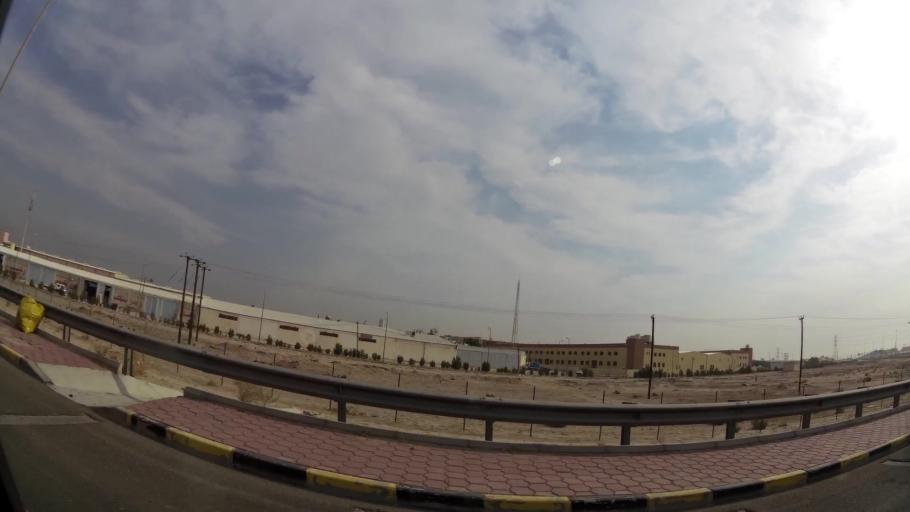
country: KW
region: Muhafazat al Jahra'
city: Al Jahra'
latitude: 29.2968
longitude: 47.7373
